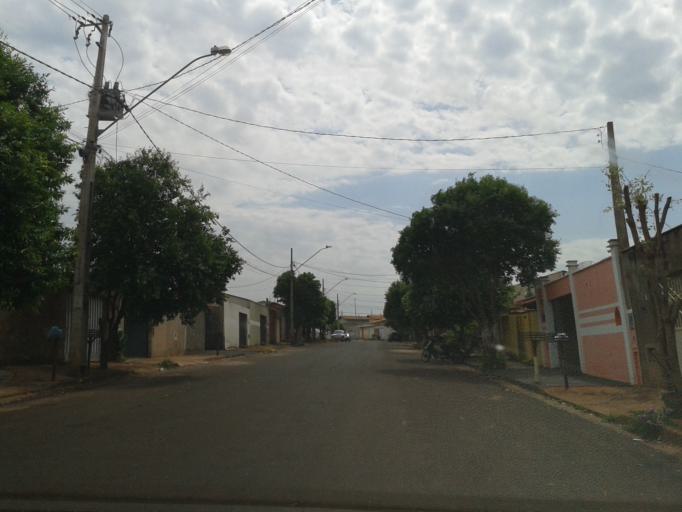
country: BR
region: Minas Gerais
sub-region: Ituiutaba
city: Ituiutaba
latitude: -18.9837
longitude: -49.4366
